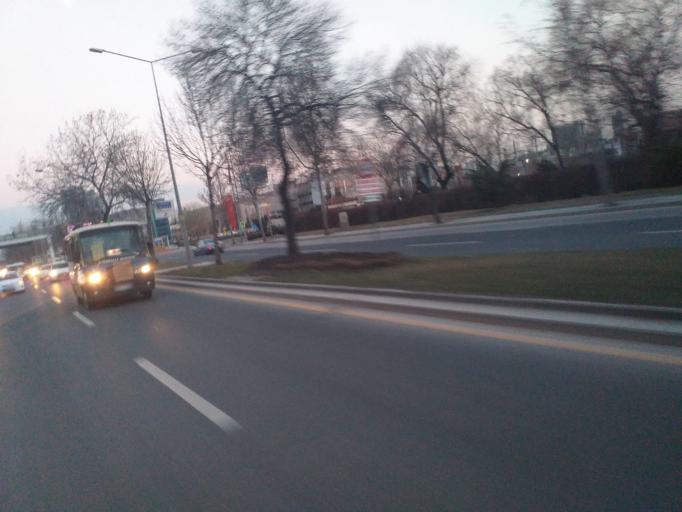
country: TR
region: Ankara
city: Ankara
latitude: 39.9490
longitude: 32.8268
